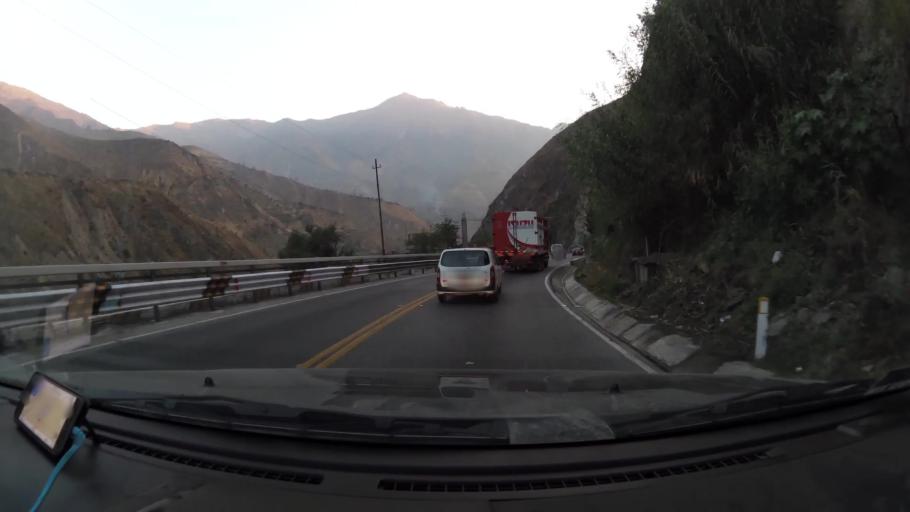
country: PE
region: Lima
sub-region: Provincia de Huarochiri
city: Surco
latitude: -11.8701
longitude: -76.4261
